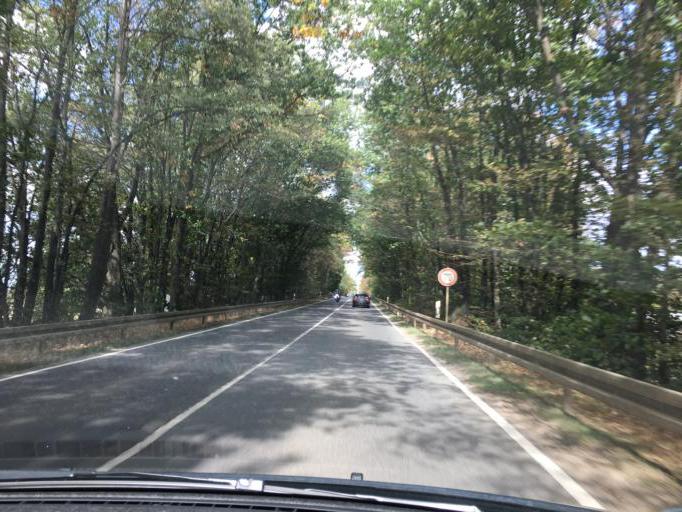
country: DE
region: North Rhine-Westphalia
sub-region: Regierungsbezirk Koln
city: Elsdorf
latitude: 50.8916
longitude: 6.6103
